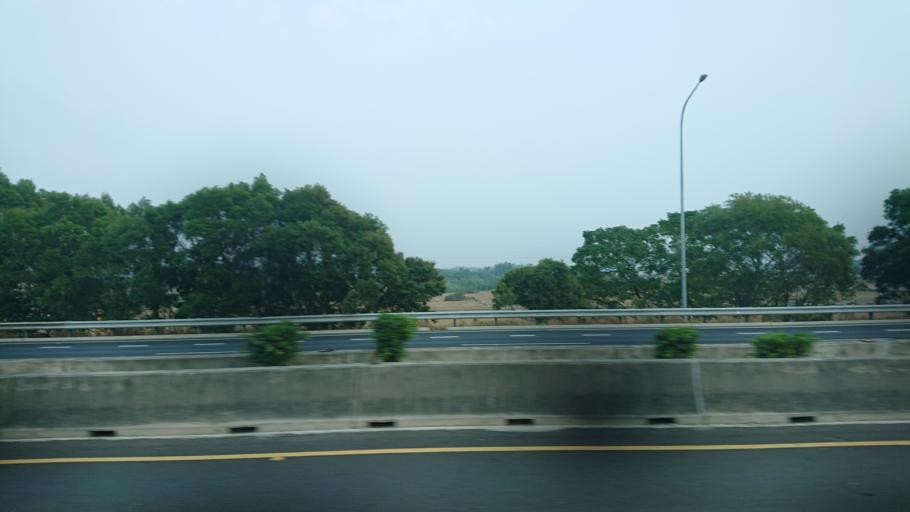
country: TW
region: Taiwan
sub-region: Chiayi
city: Jiayi Shi
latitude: 23.6177
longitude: 120.4380
